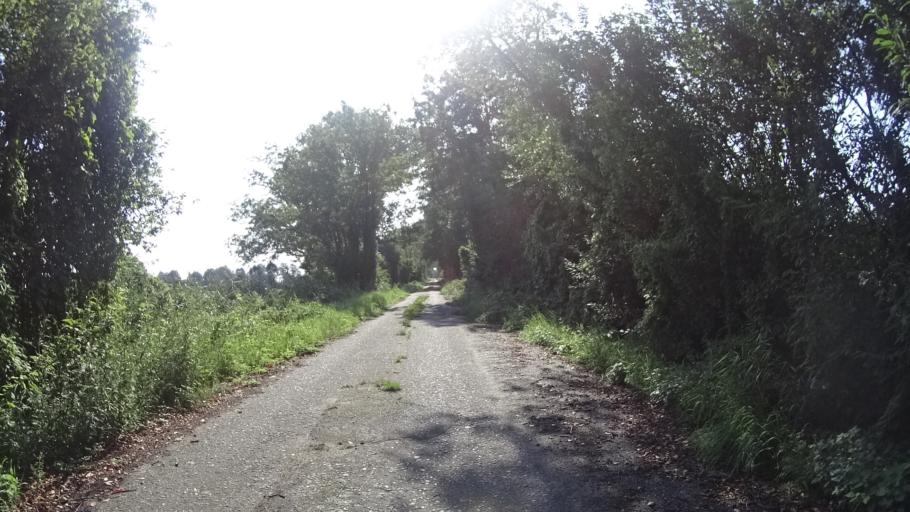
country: DE
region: Brandenburg
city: Neu Zauche
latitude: 51.9100
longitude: 14.0580
